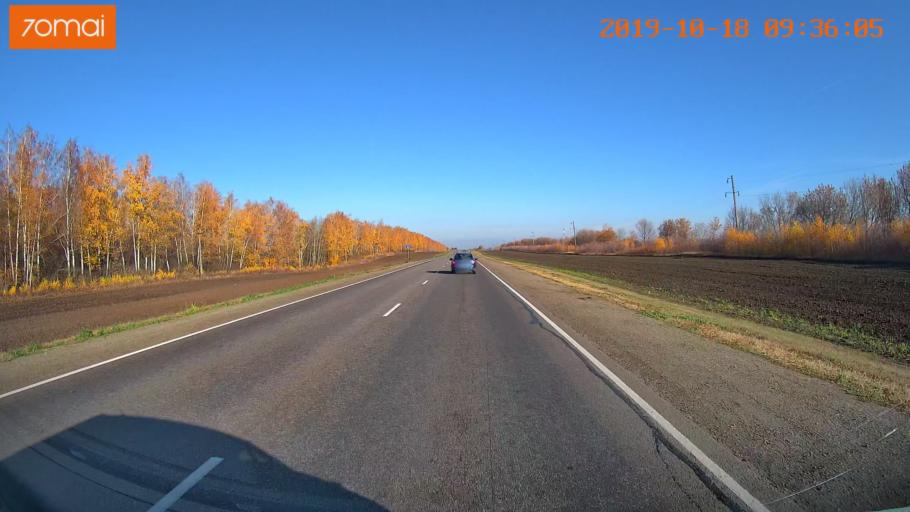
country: RU
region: Tula
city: Yefremov
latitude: 53.2009
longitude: 38.1464
